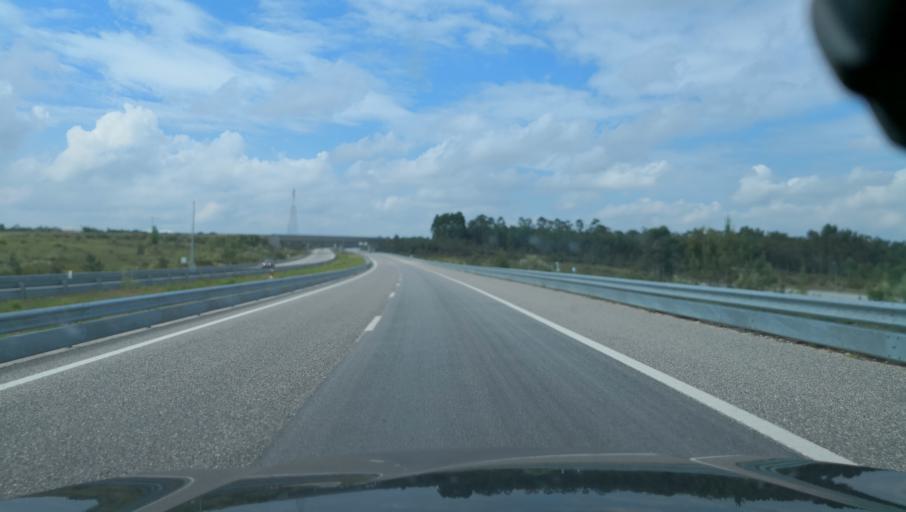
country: PT
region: Leiria
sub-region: Marinha Grande
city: Marinha Grande
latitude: 39.7431
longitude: -8.8839
